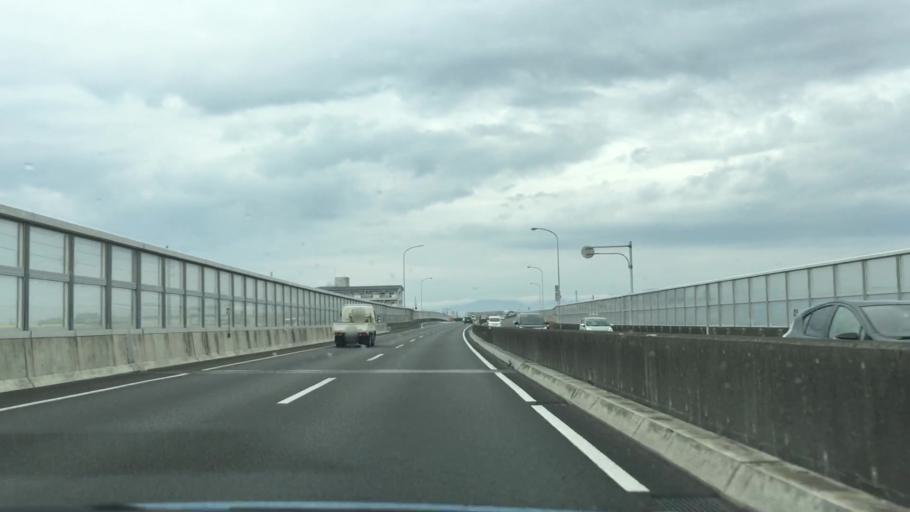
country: JP
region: Aichi
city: Toyohashi
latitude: 34.7358
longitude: 137.3469
